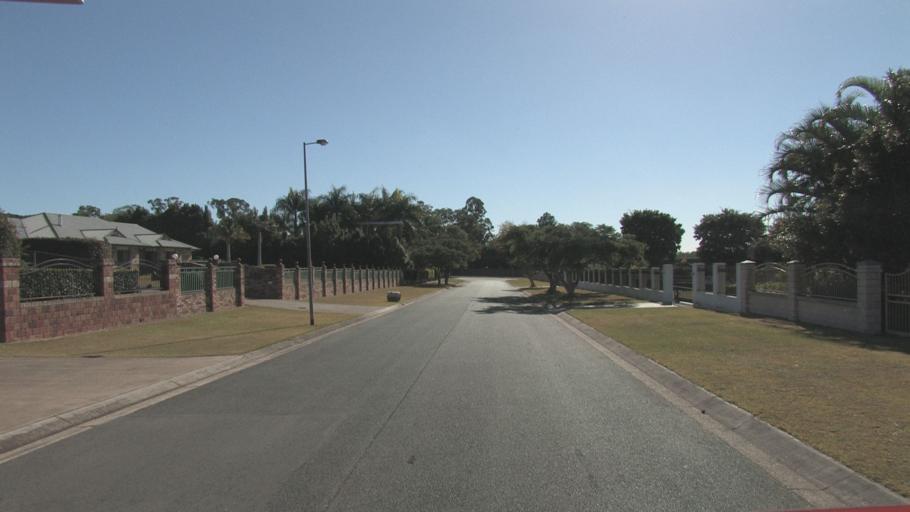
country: AU
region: Queensland
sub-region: Brisbane
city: Forest Lake
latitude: -27.6646
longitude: 153.0141
